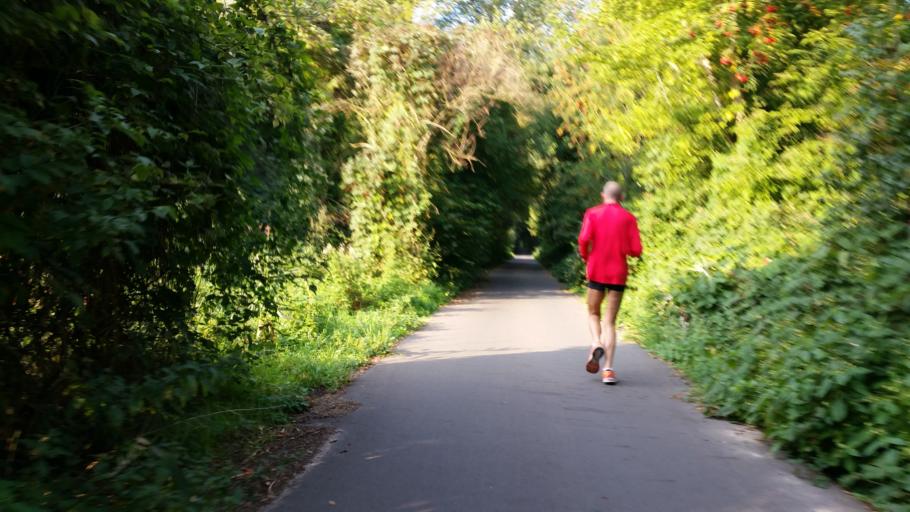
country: DE
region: Berlin
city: Lichterfelde
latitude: 52.4113
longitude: 13.2889
